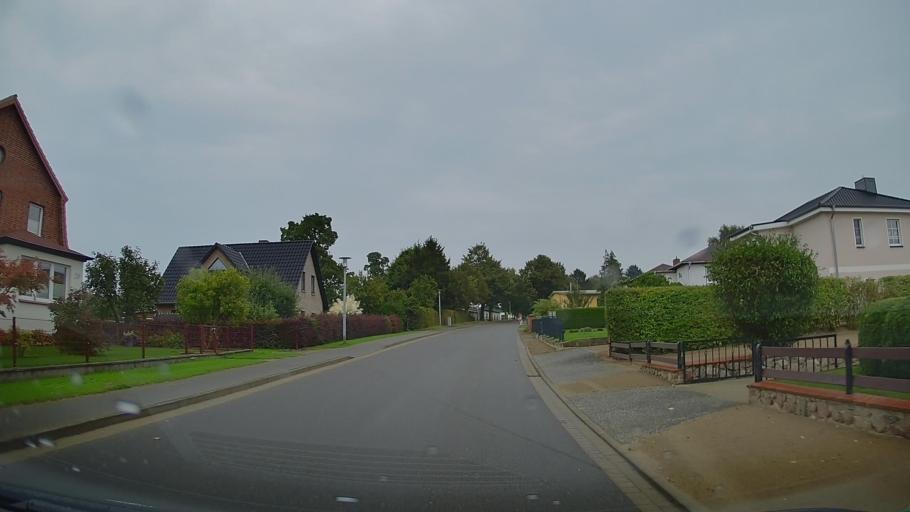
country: DE
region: Mecklenburg-Vorpommern
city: Kalkhorst
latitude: 54.0008
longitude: 11.0825
